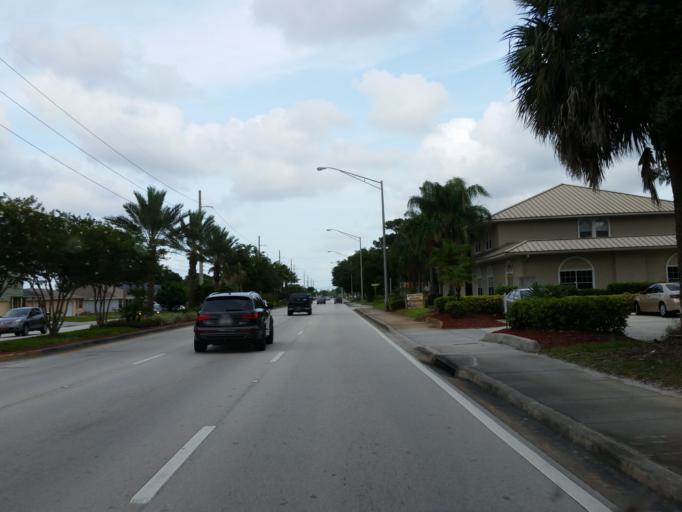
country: US
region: Florida
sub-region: Saint Lucie County
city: Port Saint Lucie
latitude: 27.2726
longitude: -80.3369
